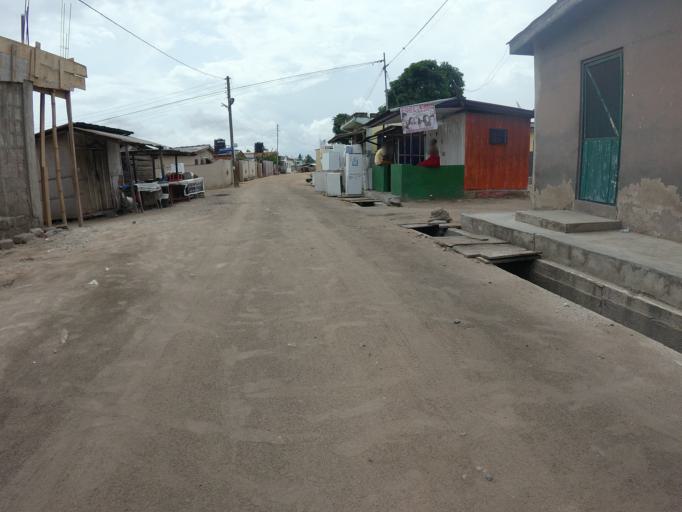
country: GH
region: Greater Accra
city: Accra
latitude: 5.6005
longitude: -0.2203
